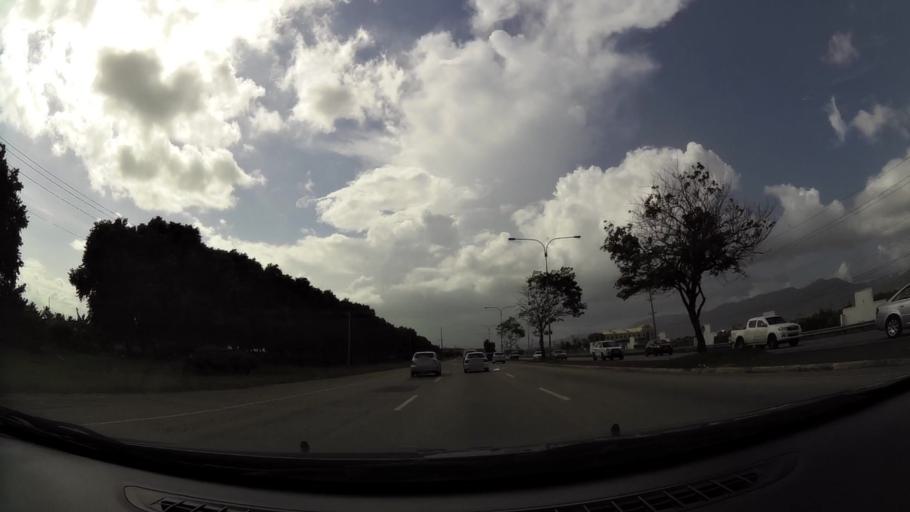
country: TT
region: Tunapuna/Piarco
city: Arouca
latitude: 10.6167
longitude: -61.3473
